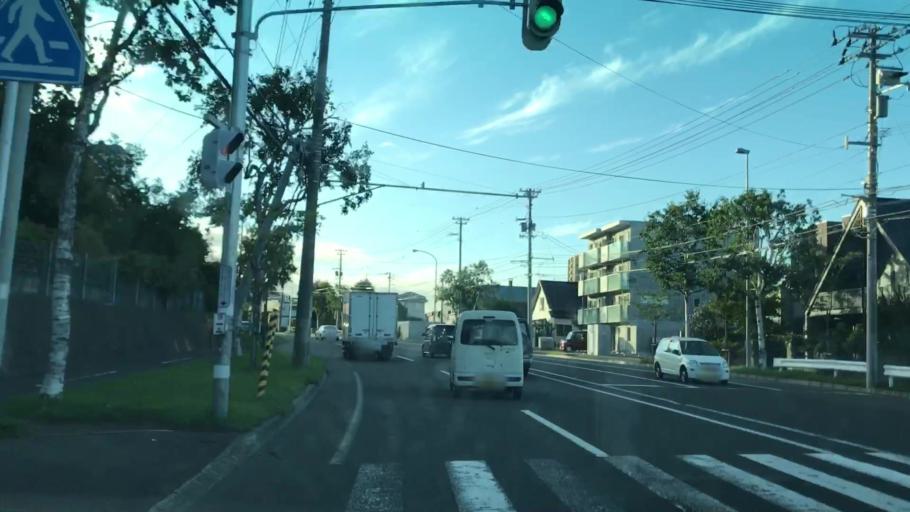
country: JP
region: Hokkaido
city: Sapporo
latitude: 43.0704
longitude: 141.2867
